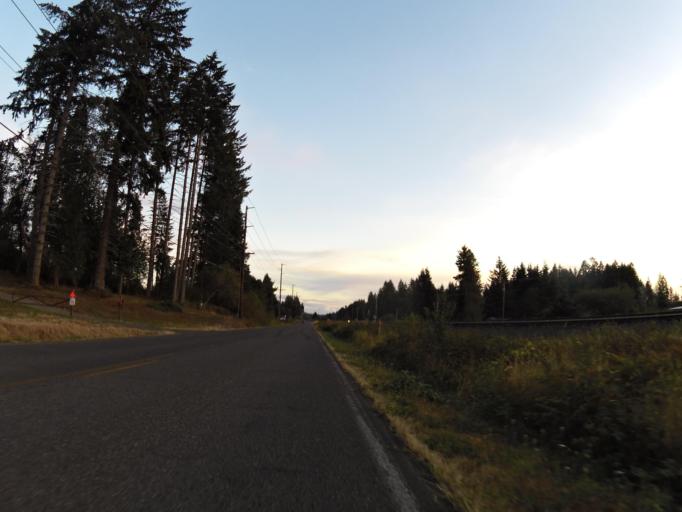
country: US
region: Washington
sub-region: Thurston County
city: Tenino
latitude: 46.8392
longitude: -122.8611
